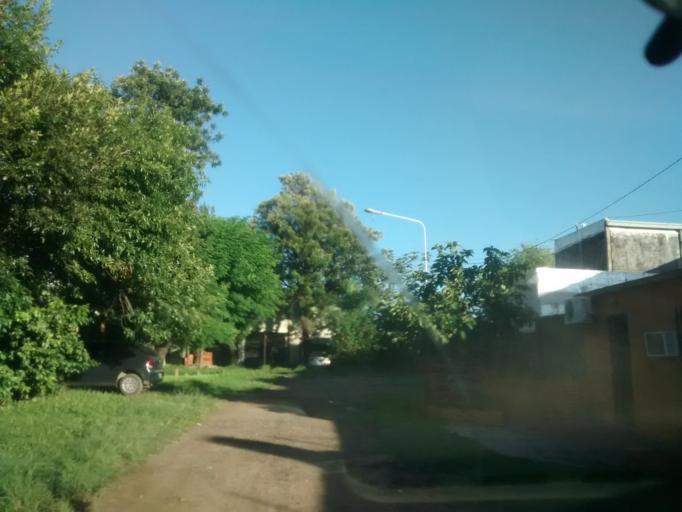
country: AR
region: Chaco
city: Fontana
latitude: -27.4483
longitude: -59.0177
